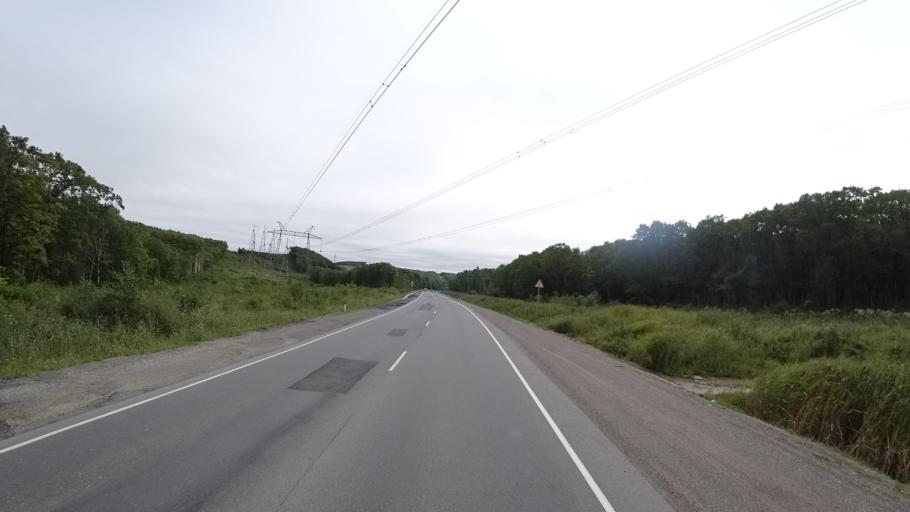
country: RU
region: Primorskiy
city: Lyalichi
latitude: 44.1070
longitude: 132.4213
